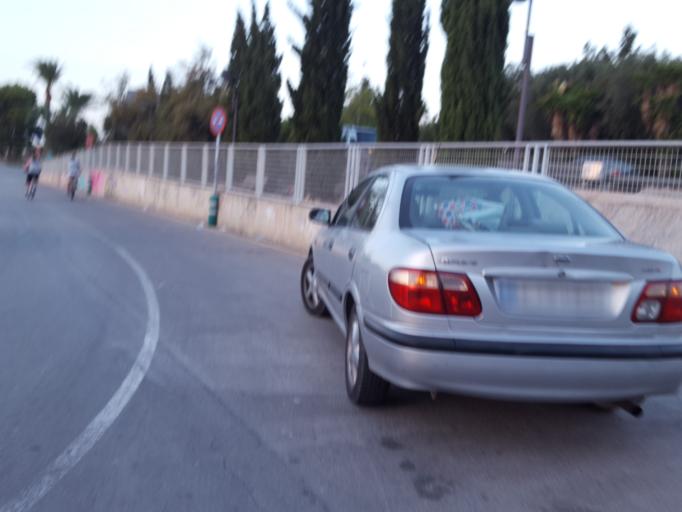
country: ES
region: Murcia
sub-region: Murcia
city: Murcia
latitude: 37.9763
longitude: -1.1376
